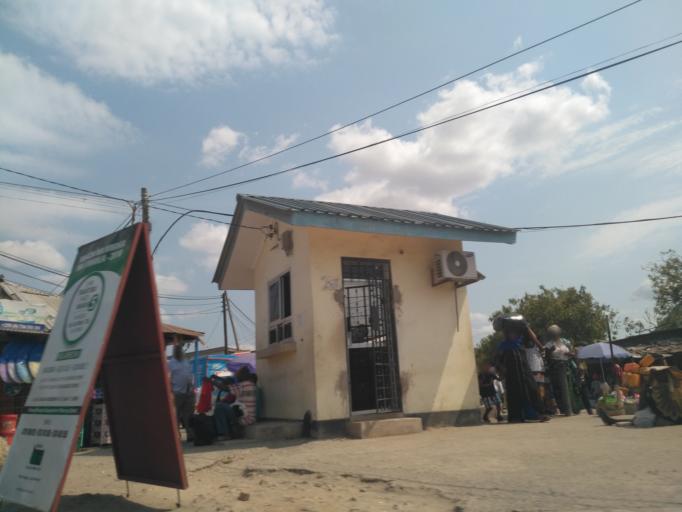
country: TZ
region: Dar es Salaam
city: Dar es Salaam
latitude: -6.8225
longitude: 39.3025
